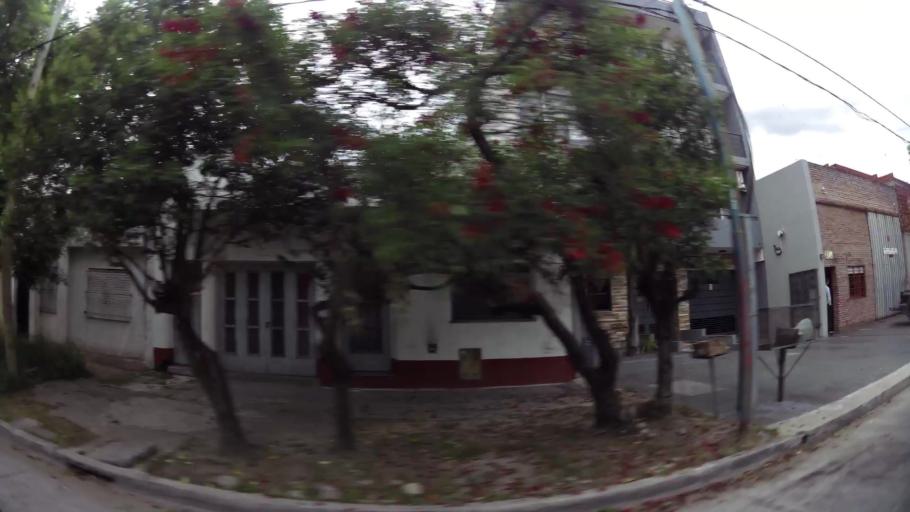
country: AR
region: Buenos Aires
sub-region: Partido de Lanus
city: Lanus
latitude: -34.6912
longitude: -58.3957
